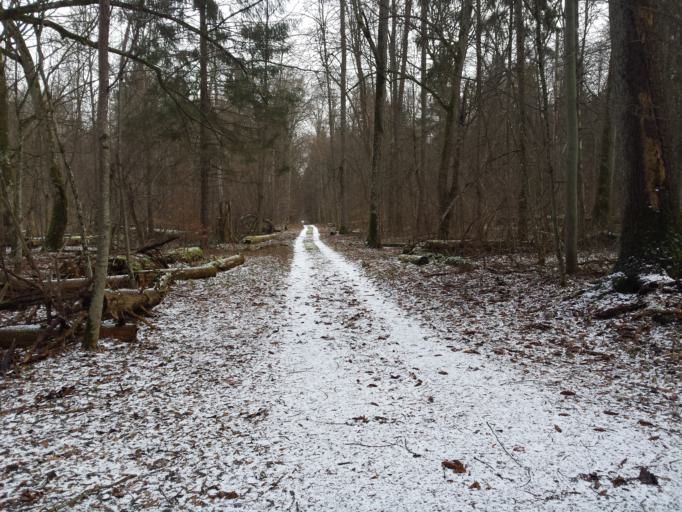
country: PL
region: Podlasie
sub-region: Powiat hajnowski
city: Bialowieza
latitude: 52.7229
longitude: 23.8438
